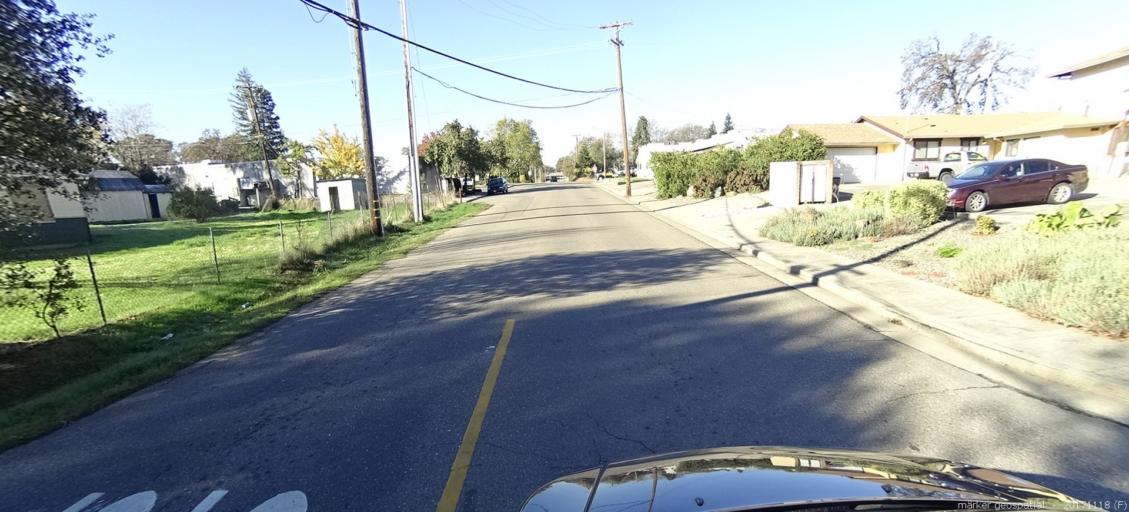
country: US
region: California
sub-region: Shasta County
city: Cottonwood
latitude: 40.3857
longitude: -122.2798
